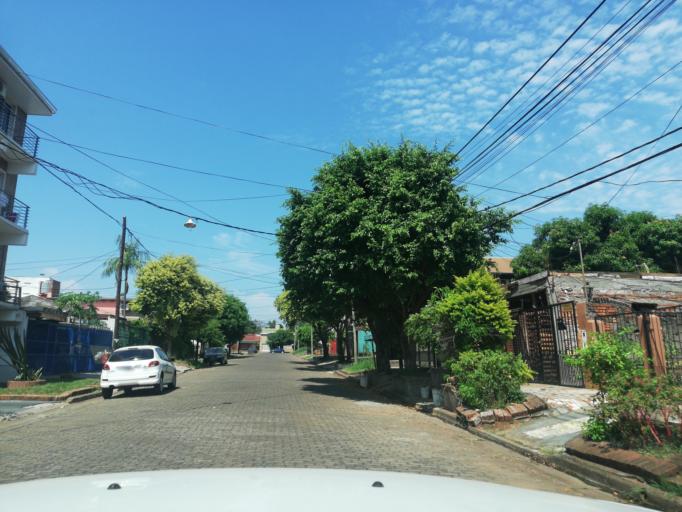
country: AR
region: Misiones
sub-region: Departamento de Capital
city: Posadas
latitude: -27.3683
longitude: -55.9104
